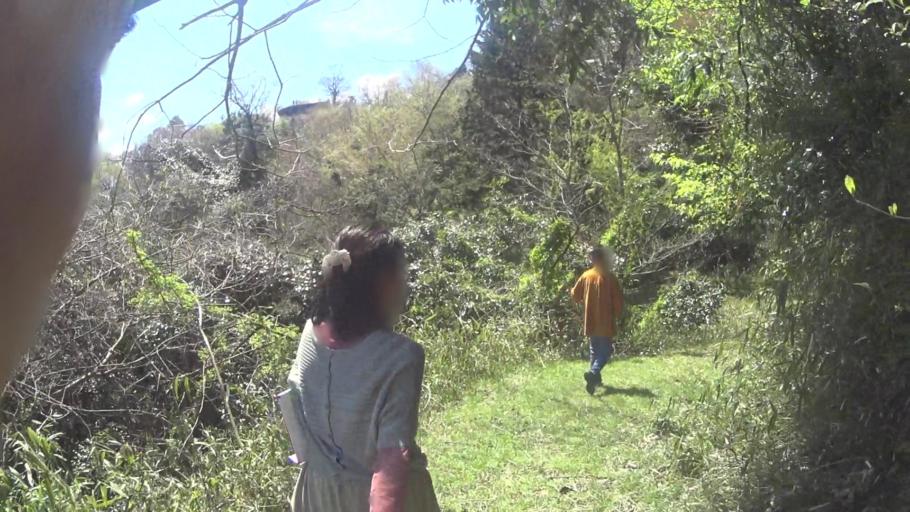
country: JP
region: Kyoto
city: Miyazu
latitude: 35.5653
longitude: 135.1369
